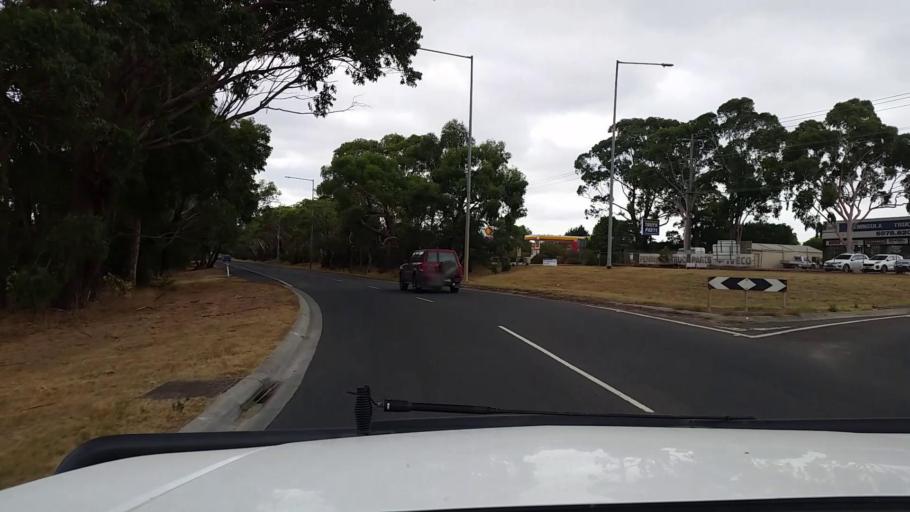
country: AU
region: Victoria
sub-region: Mornington Peninsula
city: Moorooduc
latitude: -38.2545
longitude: 145.0788
